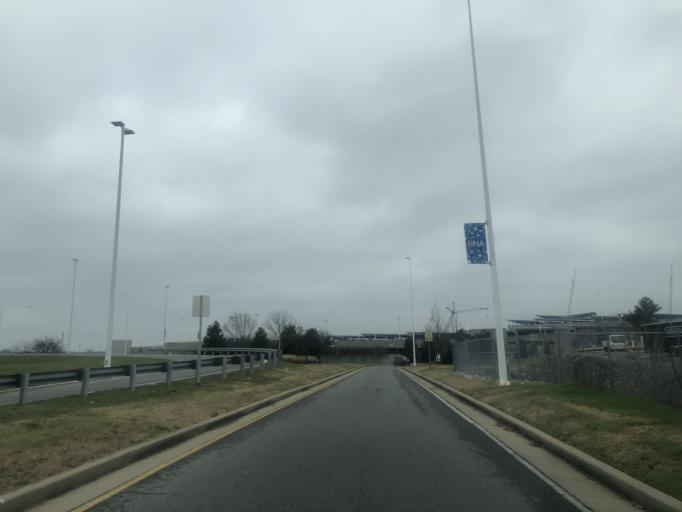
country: US
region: Tennessee
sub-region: Davidson County
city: Lakewood
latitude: 36.1365
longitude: -86.6685
